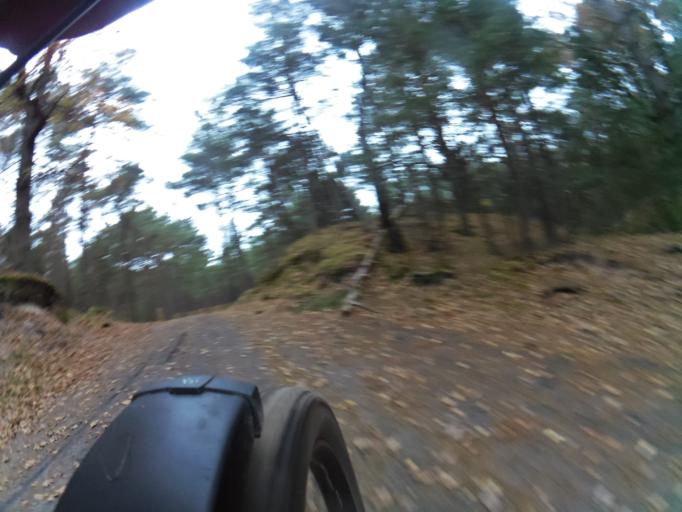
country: PL
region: Pomeranian Voivodeship
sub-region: Powiat wejherowski
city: Choczewo
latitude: 54.7835
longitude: 17.7430
